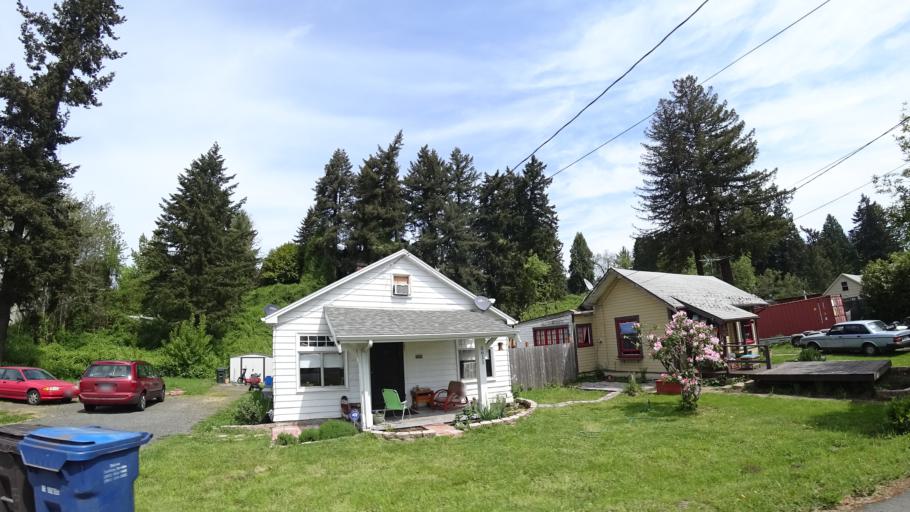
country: US
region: Oregon
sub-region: Clackamas County
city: Milwaukie
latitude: 45.4582
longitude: -122.6056
